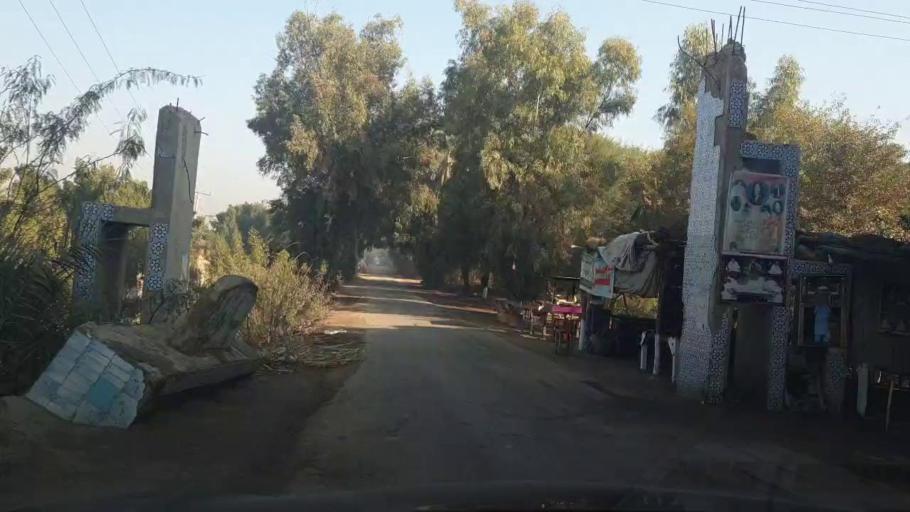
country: PK
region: Sindh
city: Mirpur Mathelo
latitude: 28.0453
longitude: 69.4592
